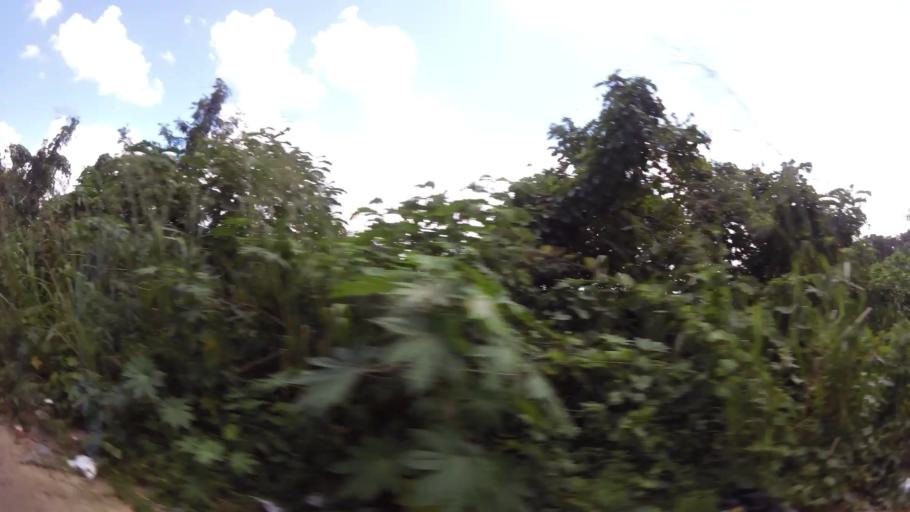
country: SR
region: Paramaribo
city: Paramaribo
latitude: 5.8611
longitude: -55.1535
